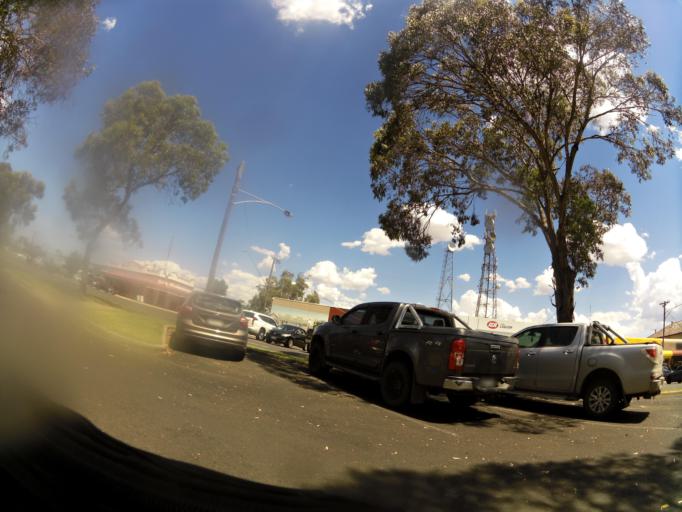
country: AU
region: Victoria
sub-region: Wellington
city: Heyfield
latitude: -37.9804
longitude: 146.7866
